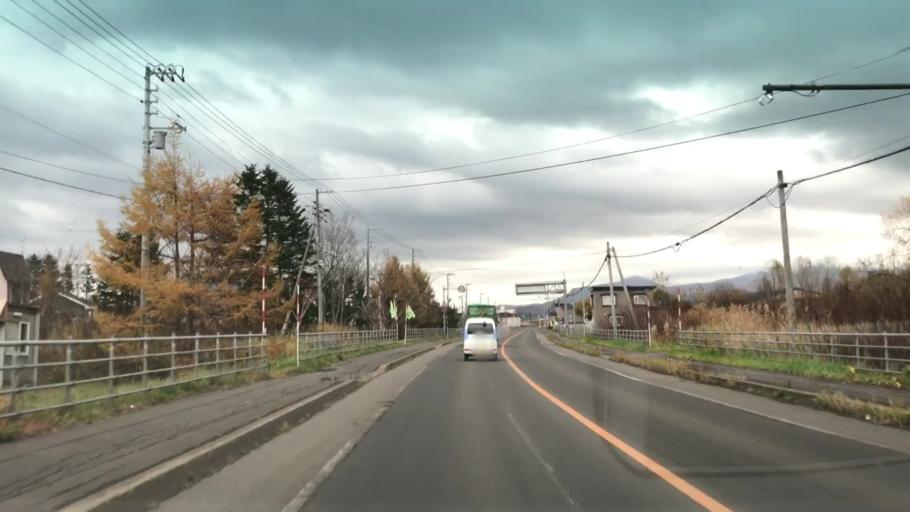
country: JP
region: Hokkaido
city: Yoichi
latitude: 43.2102
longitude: 140.7588
